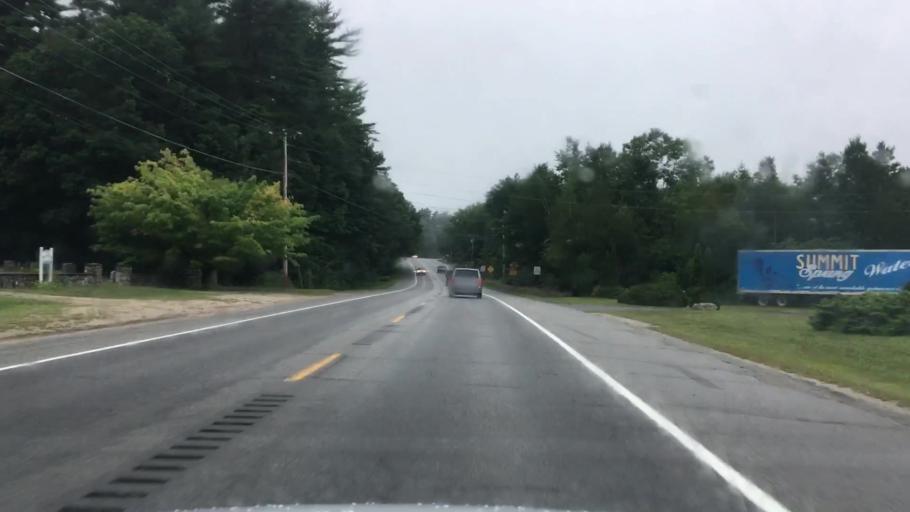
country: US
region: Maine
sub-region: Cumberland County
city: Raymond
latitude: 43.9127
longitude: -70.5131
